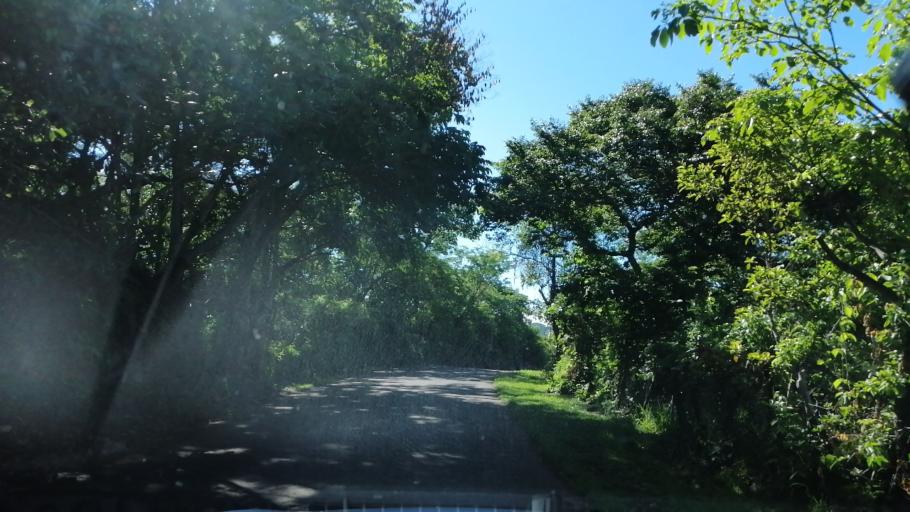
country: SV
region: Morazan
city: Corinto
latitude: 13.8105
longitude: -87.9892
